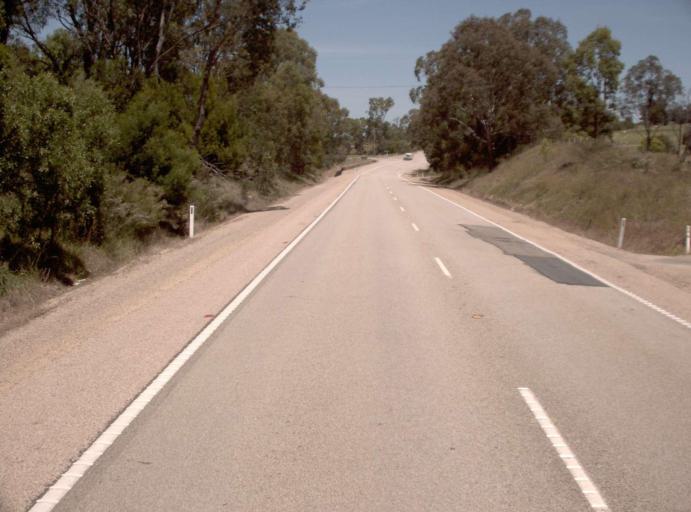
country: AU
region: Victoria
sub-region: East Gippsland
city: Bairnsdale
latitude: -37.7173
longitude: 147.8054
